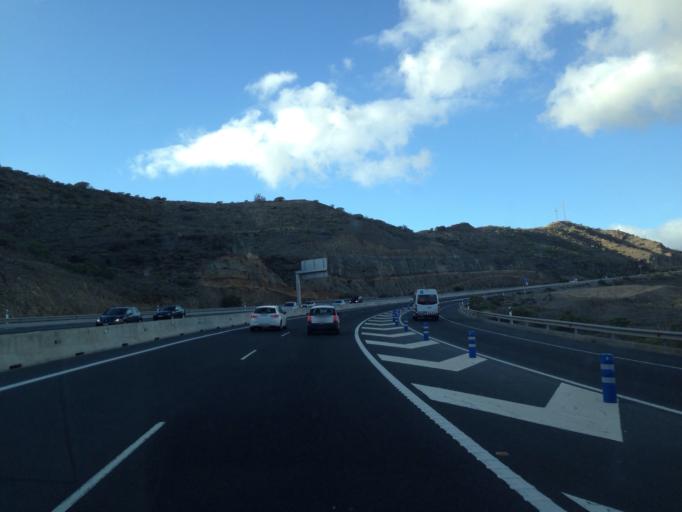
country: ES
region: Canary Islands
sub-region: Provincia de Las Palmas
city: Puerto Rico
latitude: 27.7665
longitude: -15.6739
